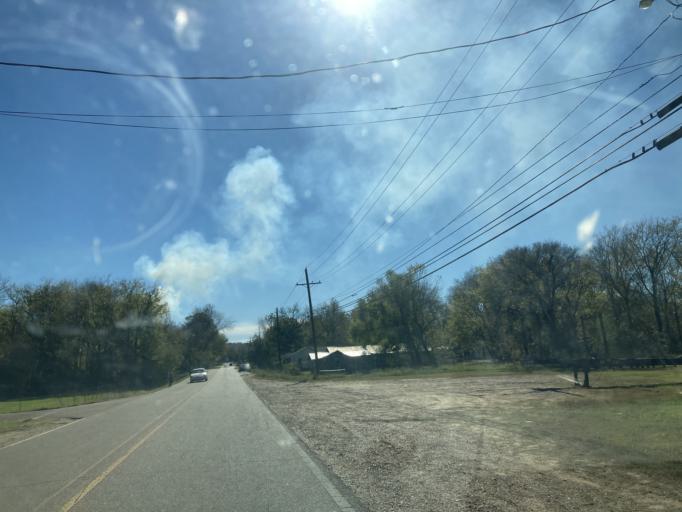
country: US
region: Mississippi
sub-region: Yazoo County
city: Yazoo City
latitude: 32.8578
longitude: -90.4112
